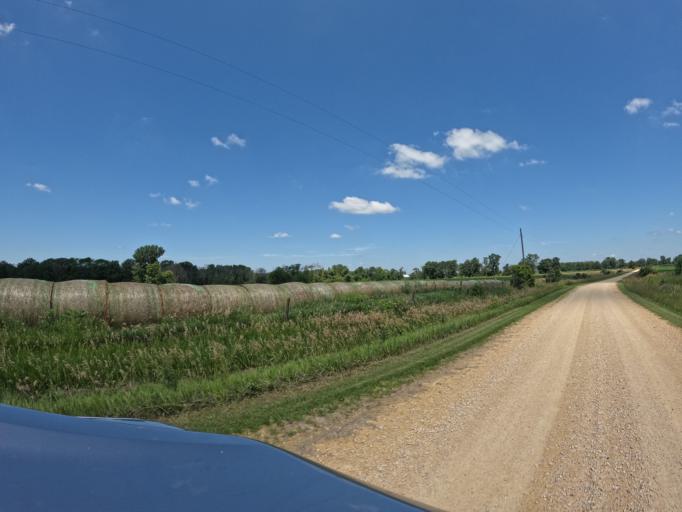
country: US
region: Iowa
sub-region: Clinton County
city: De Witt
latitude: 41.7751
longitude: -90.4297
